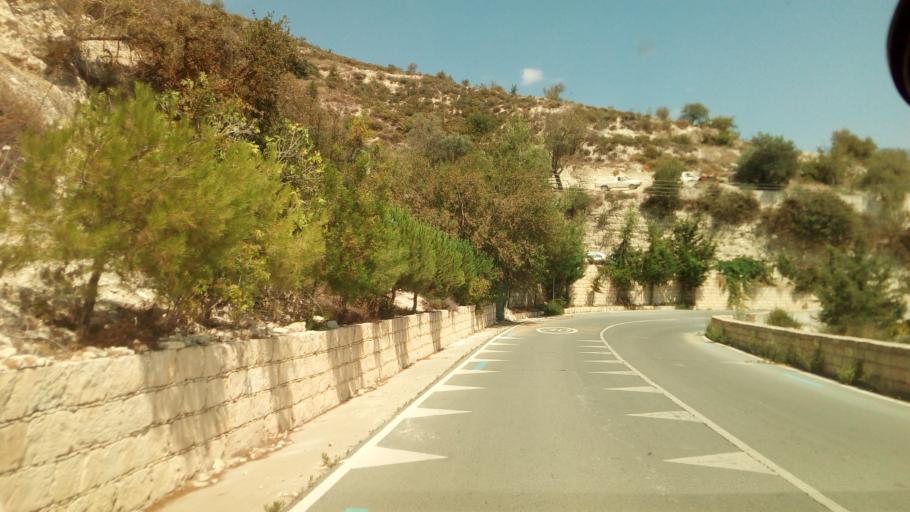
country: CY
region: Limassol
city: Pachna
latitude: 34.8258
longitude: 32.8327
